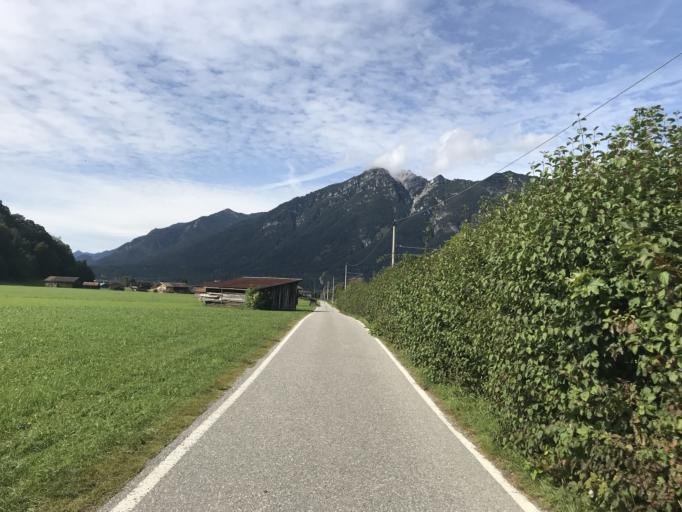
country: DE
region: Bavaria
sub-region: Upper Bavaria
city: Garmisch-Partenkirchen
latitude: 47.4835
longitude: 11.1102
